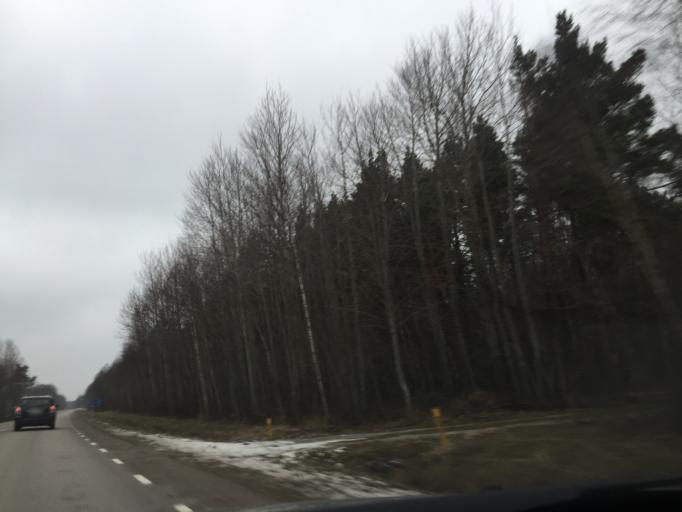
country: EE
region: Saare
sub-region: Kuressaare linn
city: Kuressaare
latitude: 58.2897
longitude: 22.3876
